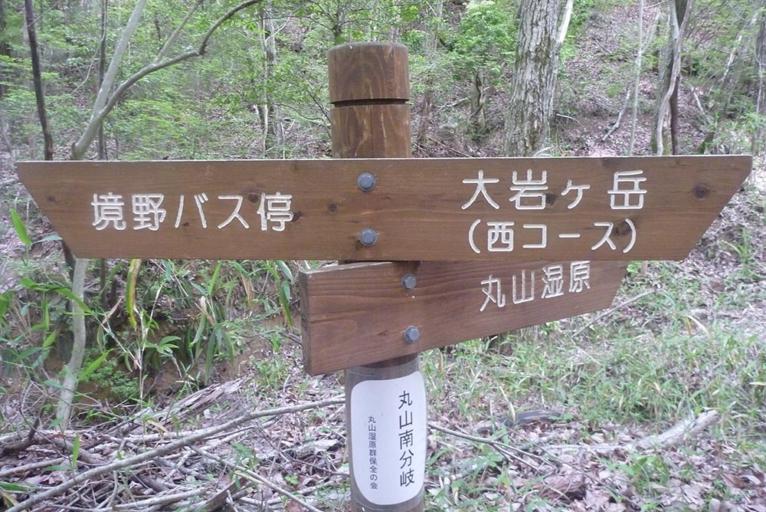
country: JP
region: Hyogo
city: Sandacho
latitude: 34.8826
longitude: 135.2878
